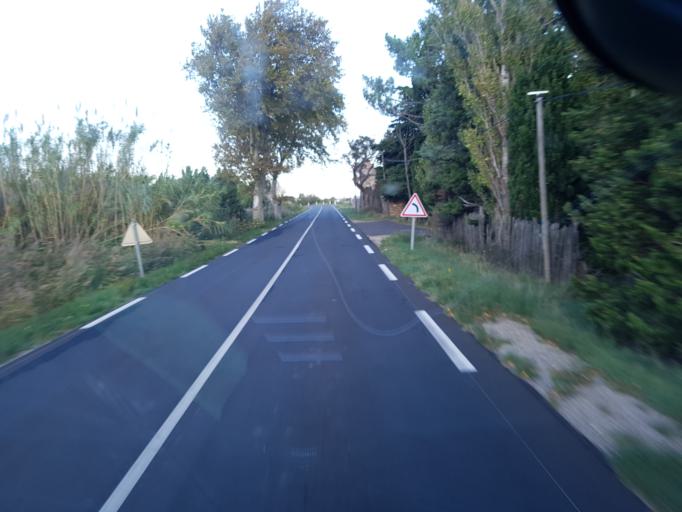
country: FR
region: Languedoc-Roussillon
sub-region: Departement de l'Aude
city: Leucate
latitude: 42.9634
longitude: 2.9938
